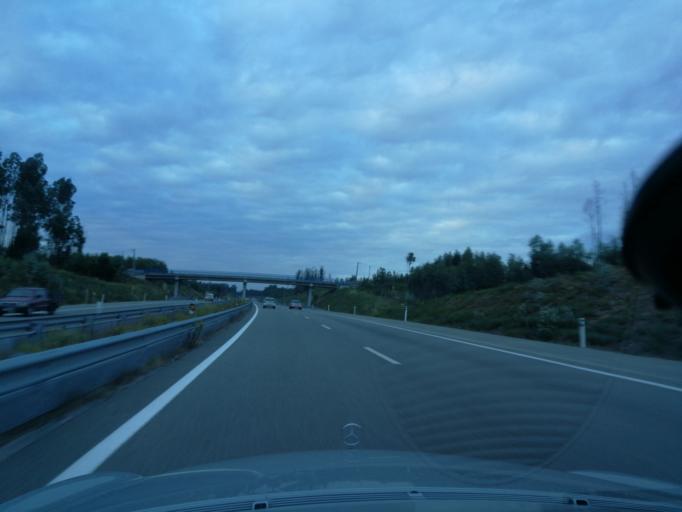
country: PT
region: Aveiro
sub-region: Estarreja
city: Salreu
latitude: 40.7087
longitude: -8.5329
